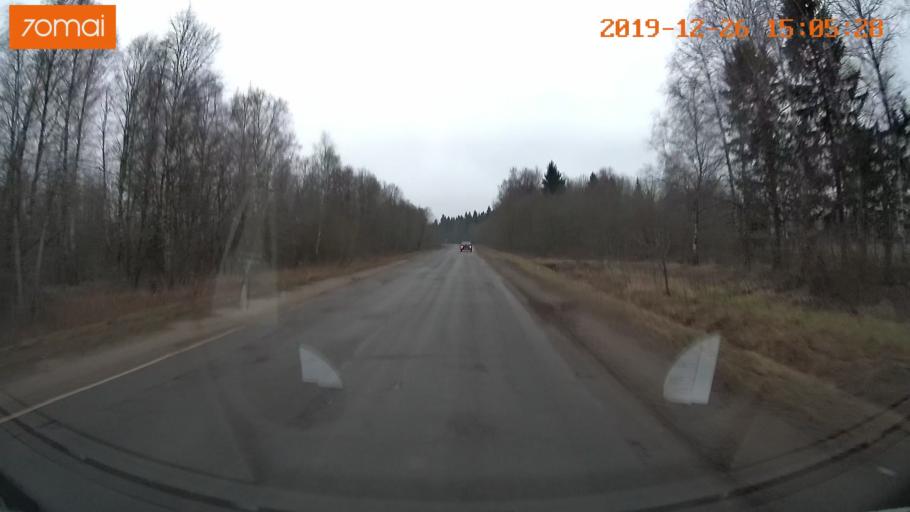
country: RU
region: Jaroslavl
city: Rybinsk
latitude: 58.1887
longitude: 38.8514
